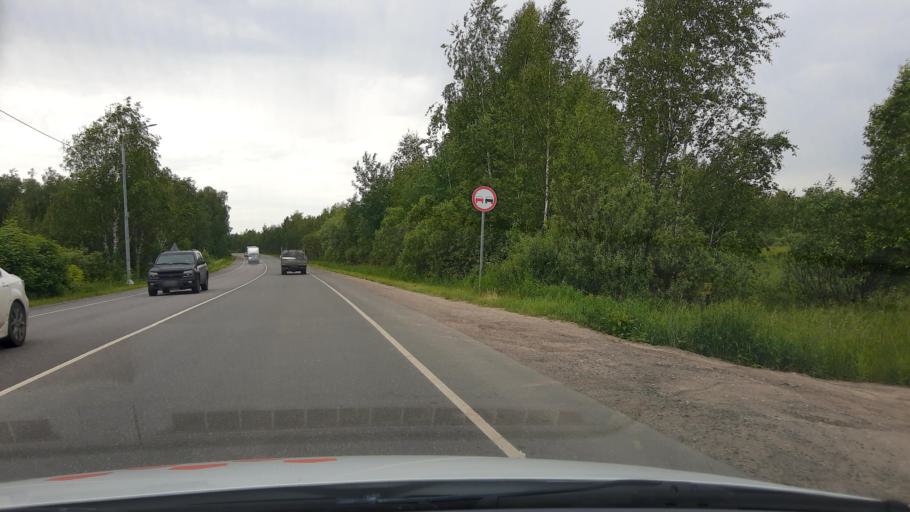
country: RU
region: Moskovskaya
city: Noginsk
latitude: 55.8670
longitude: 38.4195
